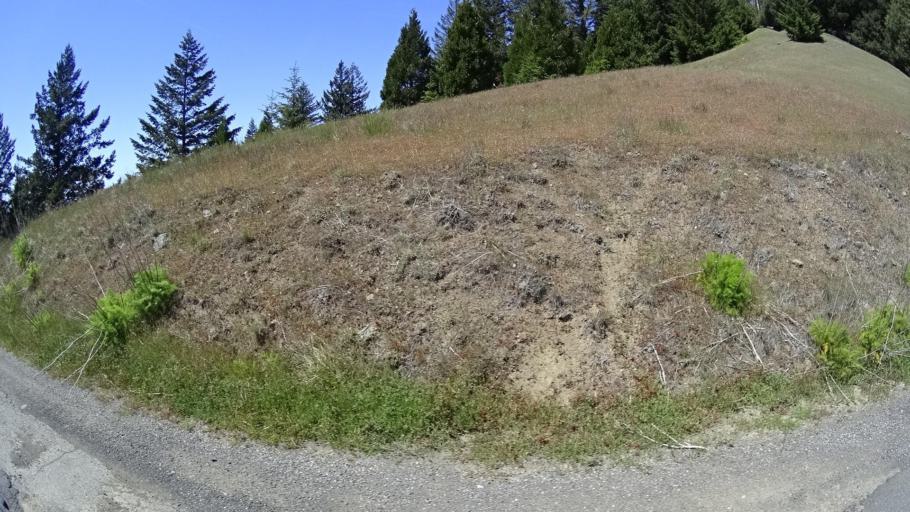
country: US
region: California
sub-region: Humboldt County
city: Rio Dell
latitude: 40.2676
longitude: -124.0866
